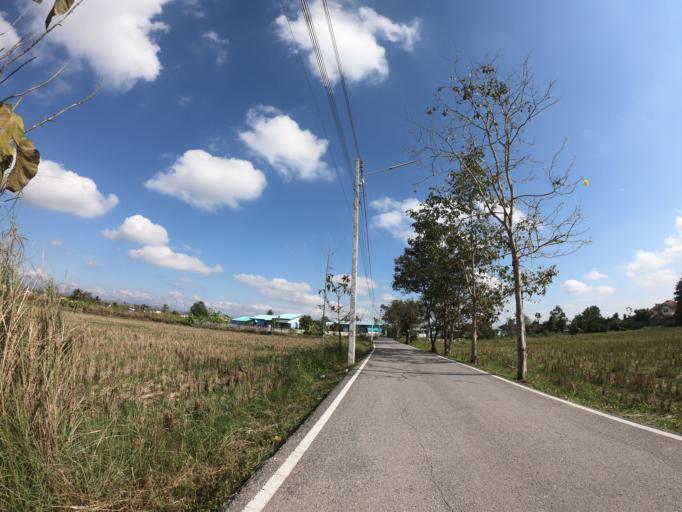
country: TH
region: Chiang Mai
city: San Sai
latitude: 18.8441
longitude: 99.0569
